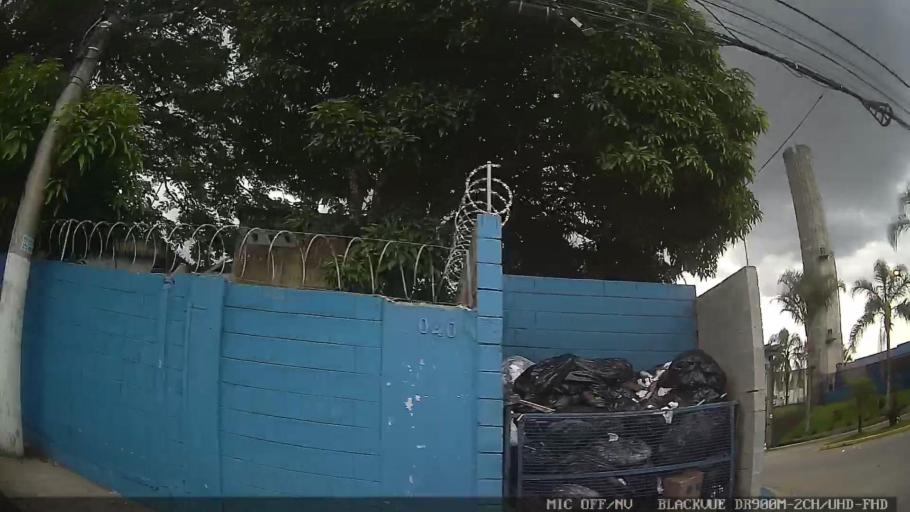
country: BR
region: Sao Paulo
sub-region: Suzano
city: Suzano
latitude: -23.5671
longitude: -46.2946
